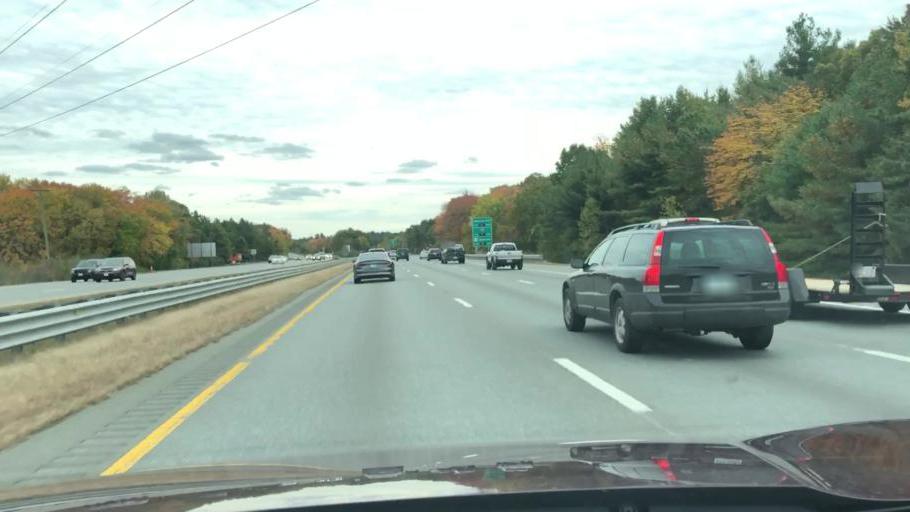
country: US
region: Massachusetts
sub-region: Middlesex County
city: Wilmington
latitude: 42.6035
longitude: -71.1716
